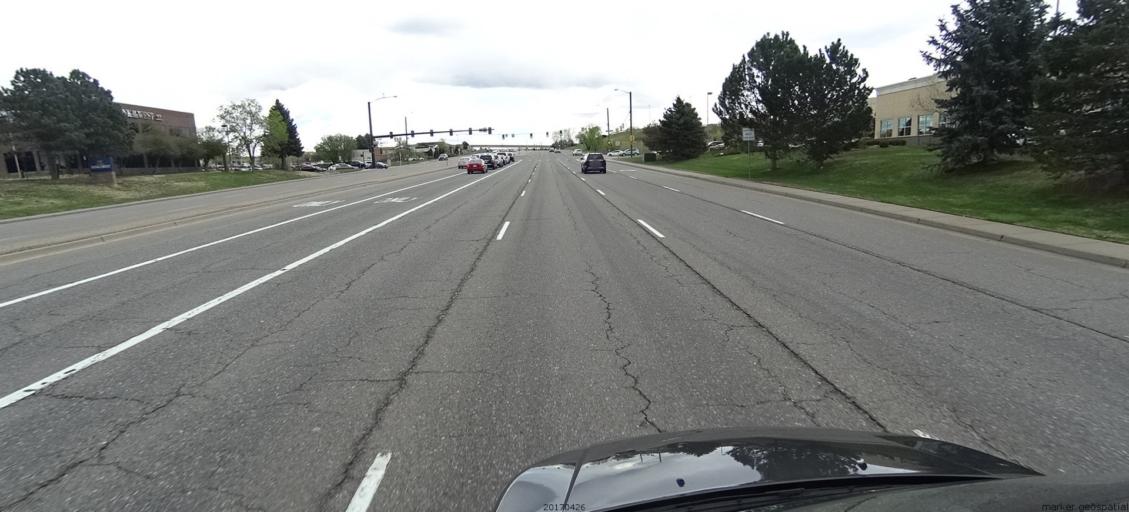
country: US
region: Colorado
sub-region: Arapahoe County
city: Centennial
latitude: 39.5659
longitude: -104.8818
